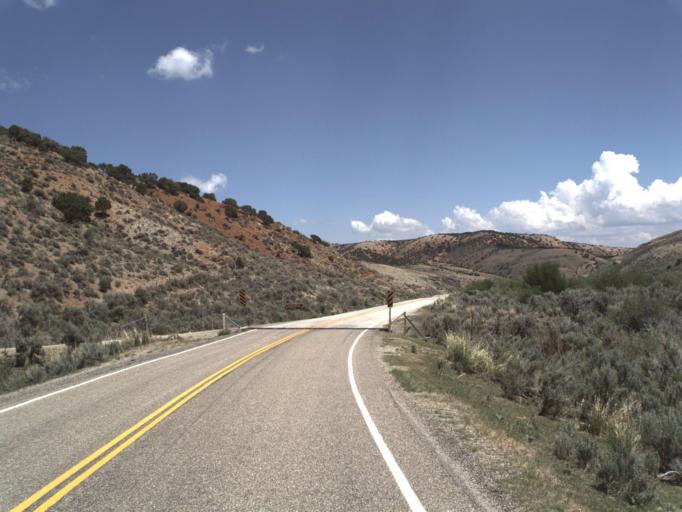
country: US
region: Utah
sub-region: Rich County
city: Randolph
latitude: 41.5031
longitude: -111.3030
